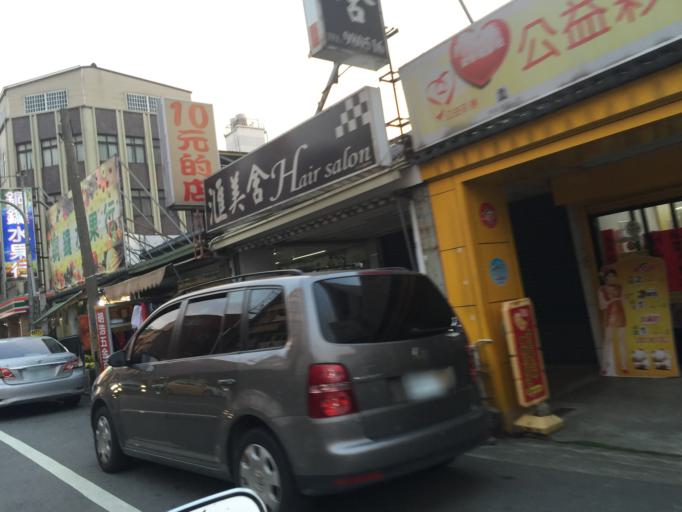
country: TW
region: Taiwan
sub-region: Miaoli
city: Miaoli
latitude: 24.4891
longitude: 120.7876
